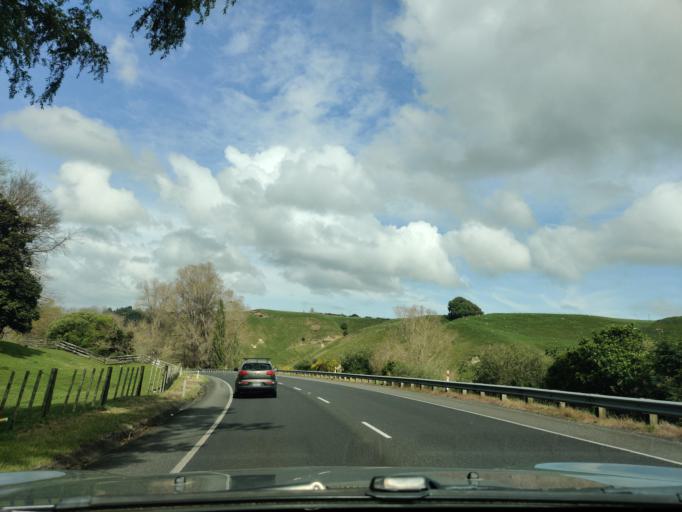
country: NZ
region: Manawatu-Wanganui
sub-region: Wanganui District
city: Wanganui
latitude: -39.8588
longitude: 174.9606
